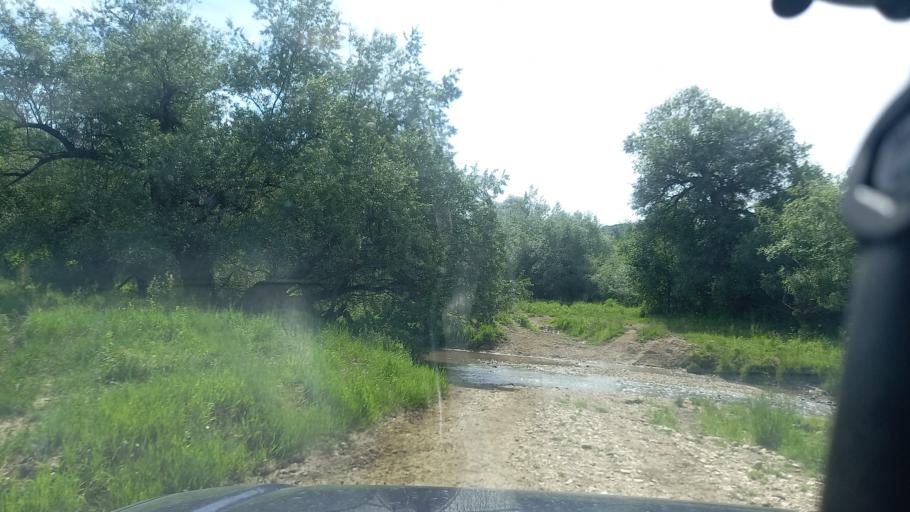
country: RU
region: Karachayevo-Cherkesiya
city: Kurdzhinovo
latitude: 44.1403
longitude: 41.0677
